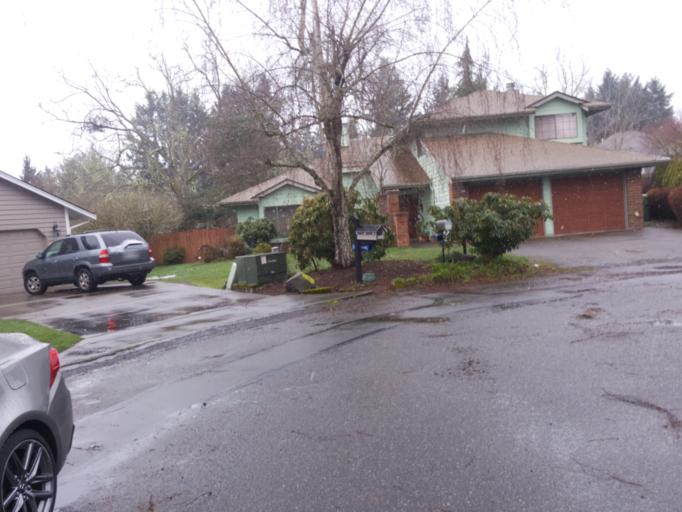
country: US
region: Washington
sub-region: Pierce County
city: University Place
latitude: 47.1977
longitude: -122.5471
